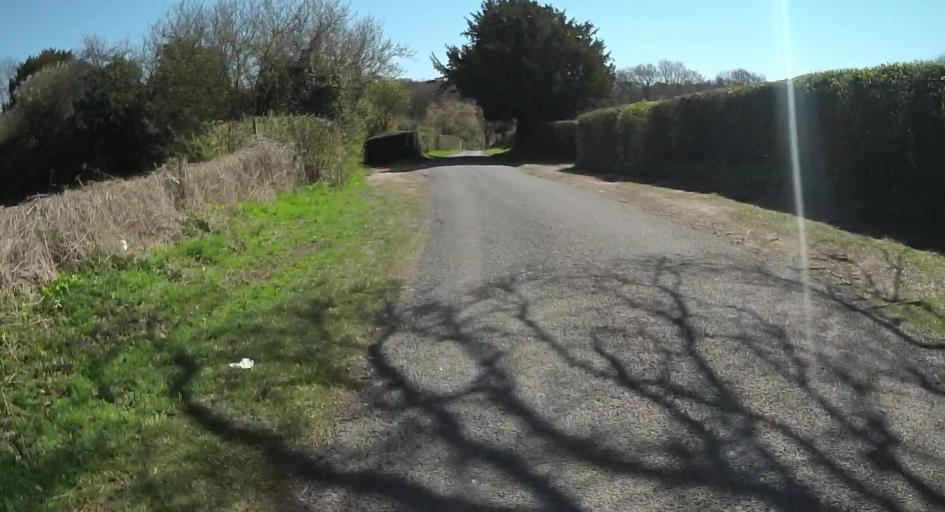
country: GB
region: England
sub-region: Hampshire
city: Old Basing
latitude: 51.2456
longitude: -1.0248
